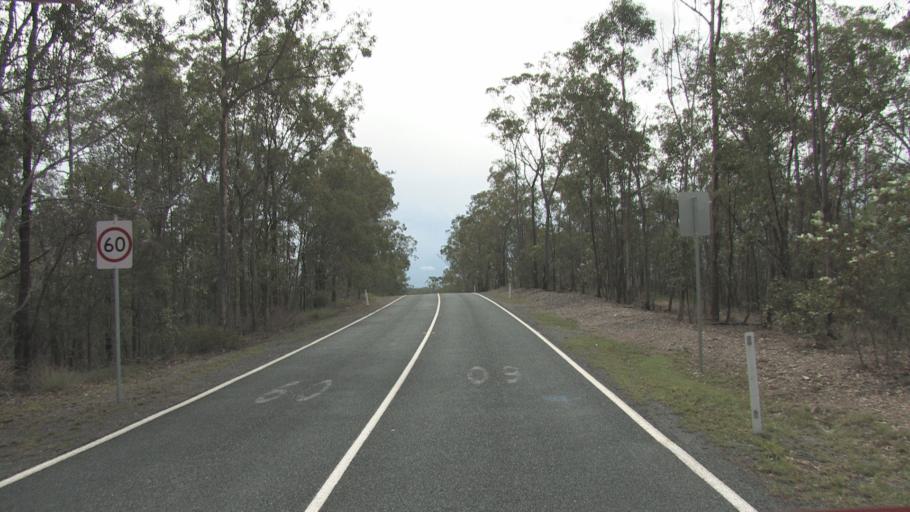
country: AU
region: Queensland
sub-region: Logan
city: Windaroo
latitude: -27.7283
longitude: 153.1829
